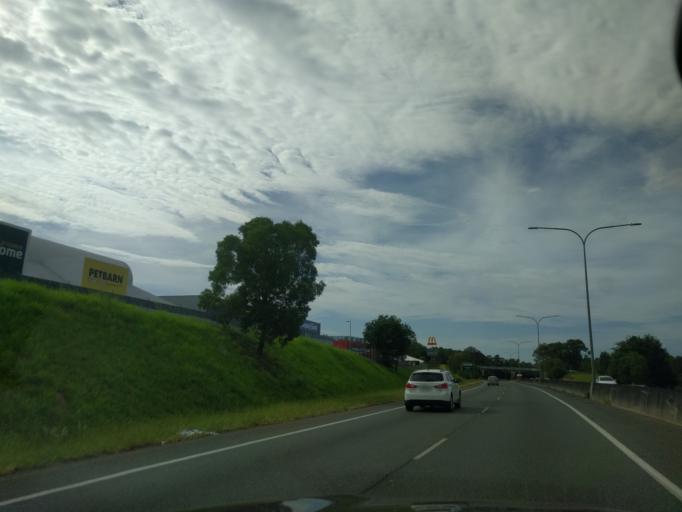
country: AU
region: Queensland
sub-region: Brisbane
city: Seventeen Mile Rocks
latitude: -27.5332
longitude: 152.9465
